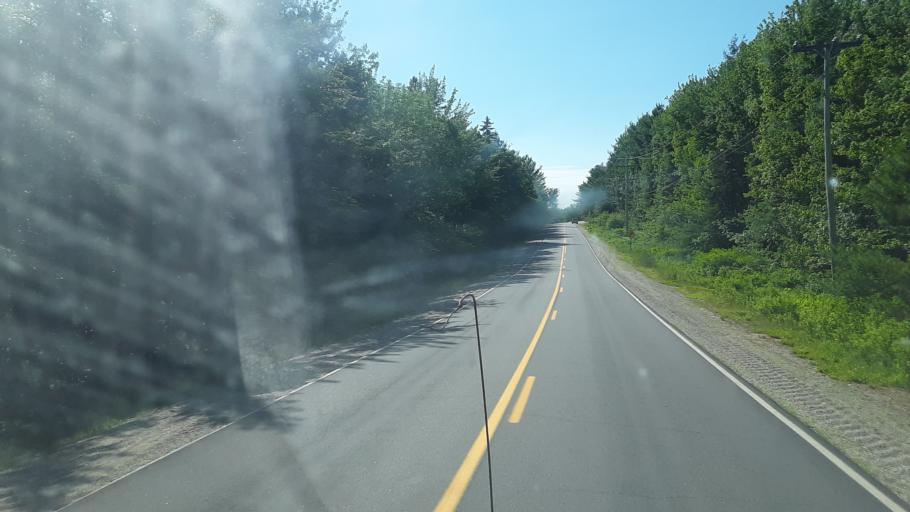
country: US
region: Maine
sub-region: Washington County
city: Cherryfield
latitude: 44.6198
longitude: -67.9309
